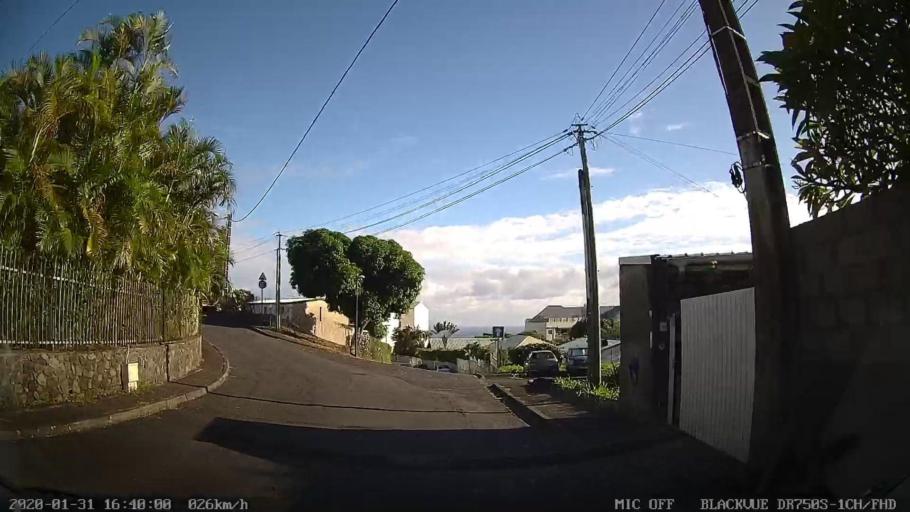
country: RE
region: Reunion
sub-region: Reunion
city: Saint-Denis
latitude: -20.9078
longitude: 55.4878
